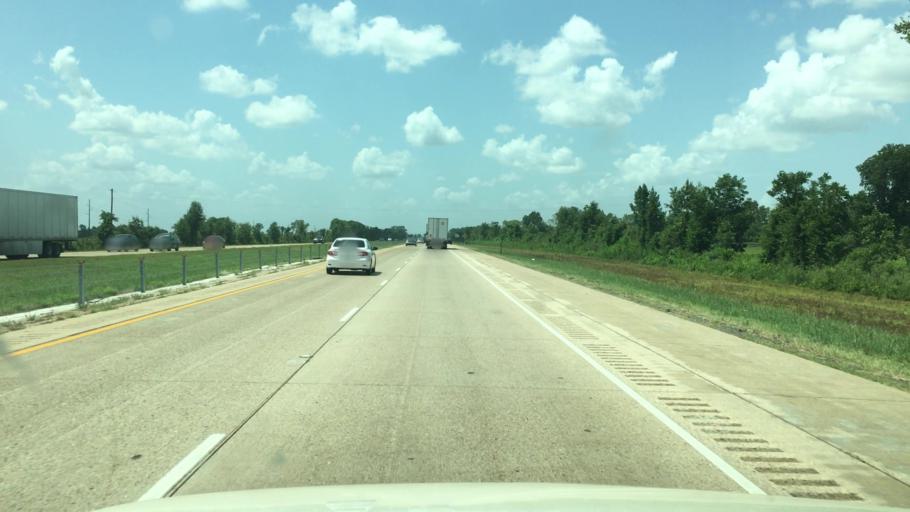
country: US
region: Arkansas
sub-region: Miller County
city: Texarkana
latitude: 33.5649
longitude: -93.8562
